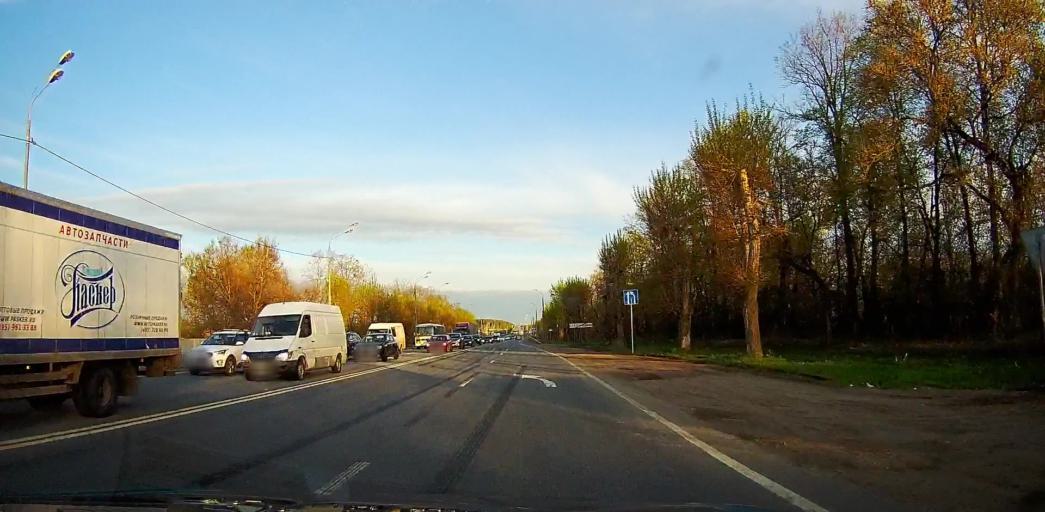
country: RU
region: Moskovskaya
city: Troitskoye
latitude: 55.2420
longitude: 38.5370
